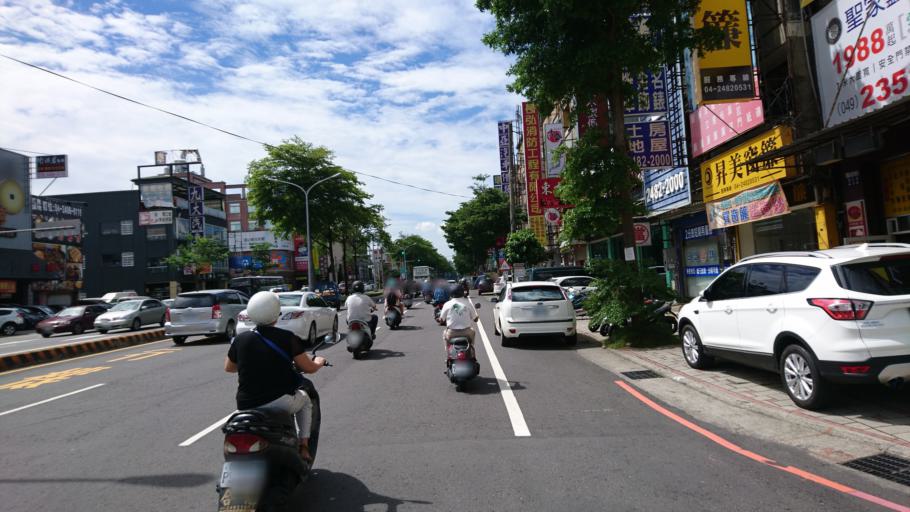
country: TW
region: Taiwan
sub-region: Taichung City
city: Taichung
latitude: 24.1050
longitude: 120.6813
